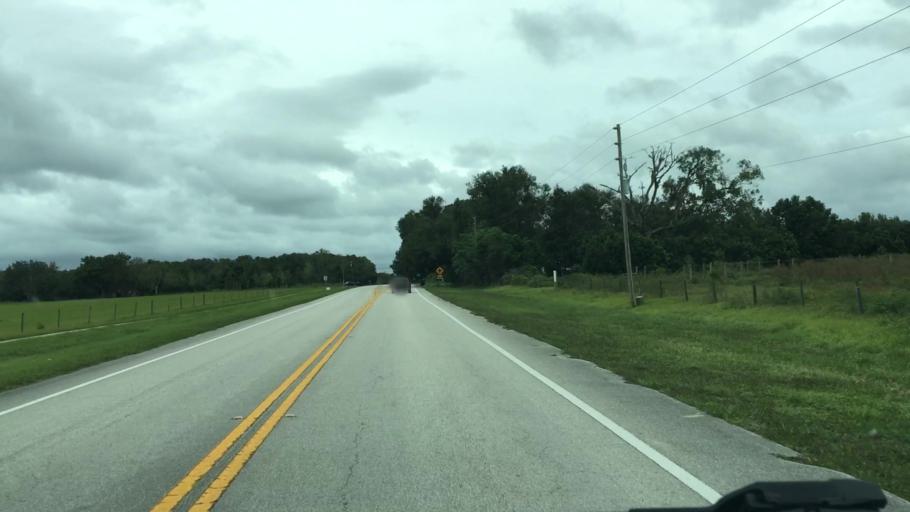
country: US
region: Florida
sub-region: Volusia County
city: Lake Helen
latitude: 28.9821
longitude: -81.2235
